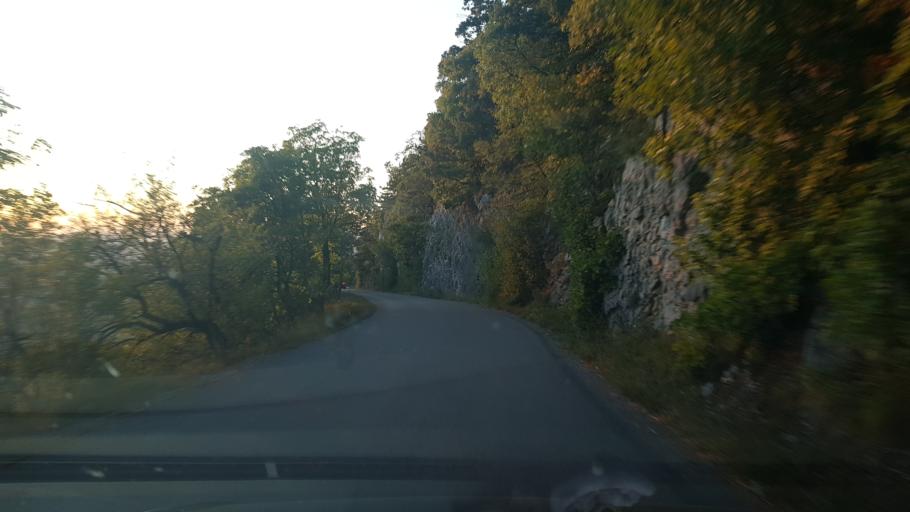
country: SI
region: Vipava
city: Vipava
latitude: 45.7949
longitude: 14.0066
